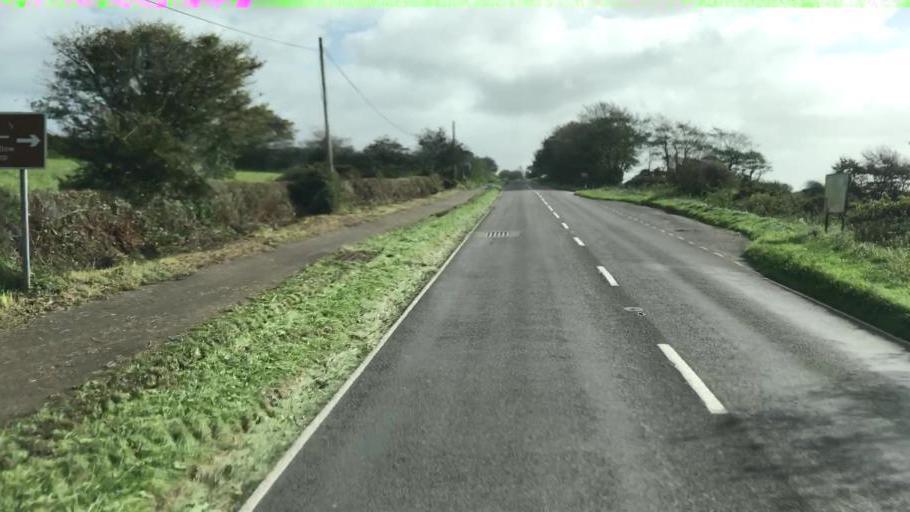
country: GB
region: England
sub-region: Cornwall
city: Callington
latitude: 50.5166
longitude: -4.2663
